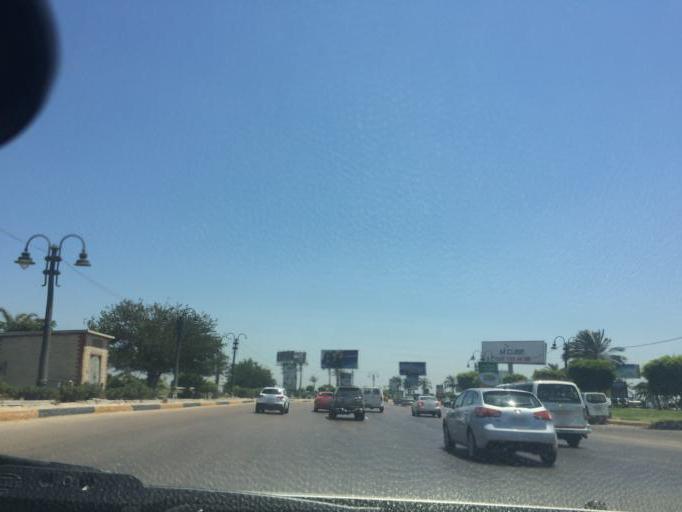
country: EG
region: Alexandria
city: Alexandria
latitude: 31.1680
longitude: 29.9349
